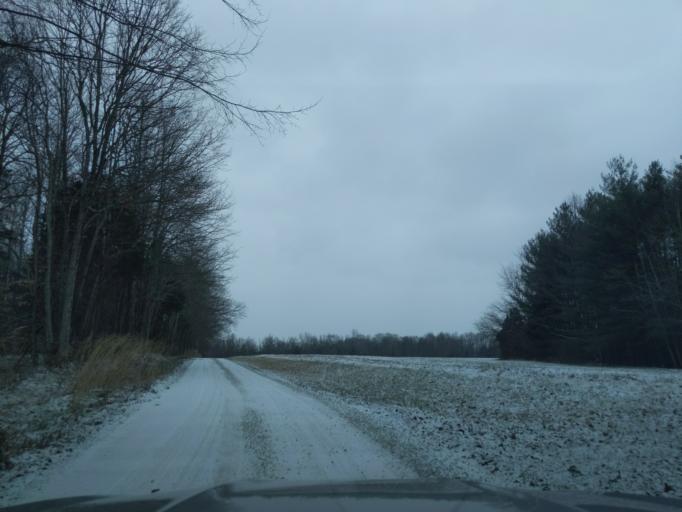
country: US
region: Indiana
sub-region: Decatur County
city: Westport
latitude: 39.2052
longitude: -85.4446
